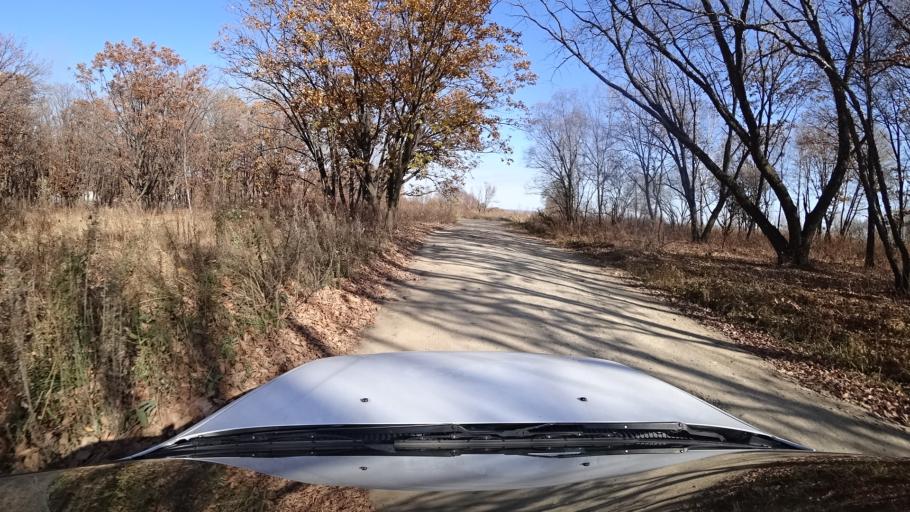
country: RU
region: Primorskiy
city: Dal'nerechensk
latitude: 45.8820
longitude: 133.7342
